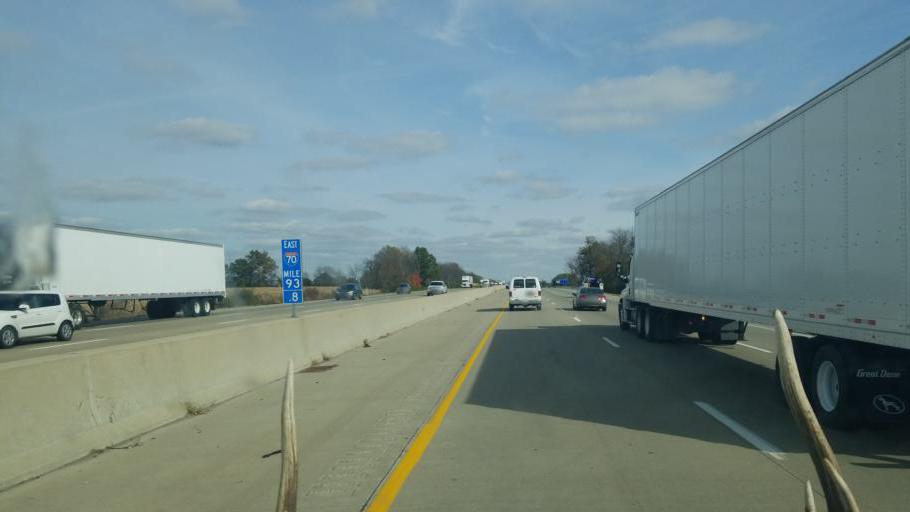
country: US
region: Indiana
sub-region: Marion County
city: Cumberland
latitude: 39.8070
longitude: -85.9525
